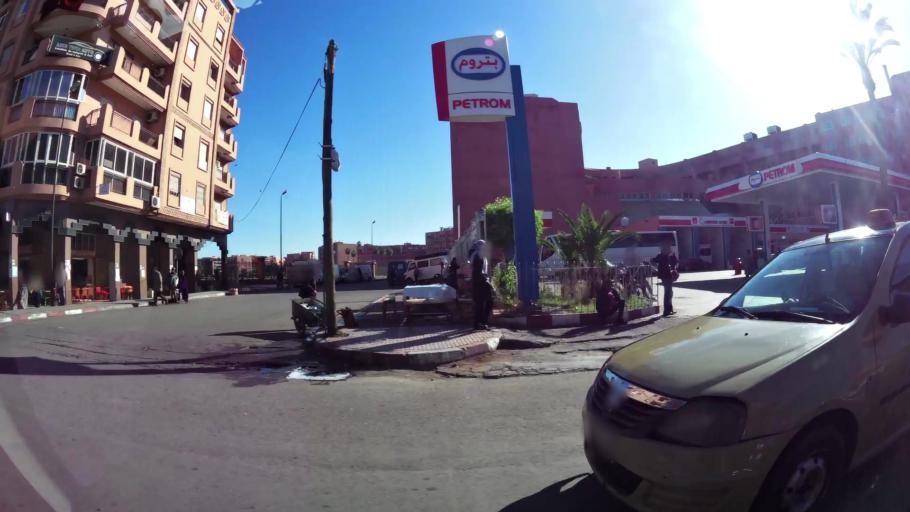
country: MA
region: Marrakech-Tensift-Al Haouz
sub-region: Marrakech
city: Marrakesh
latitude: 31.6367
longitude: -8.0013
